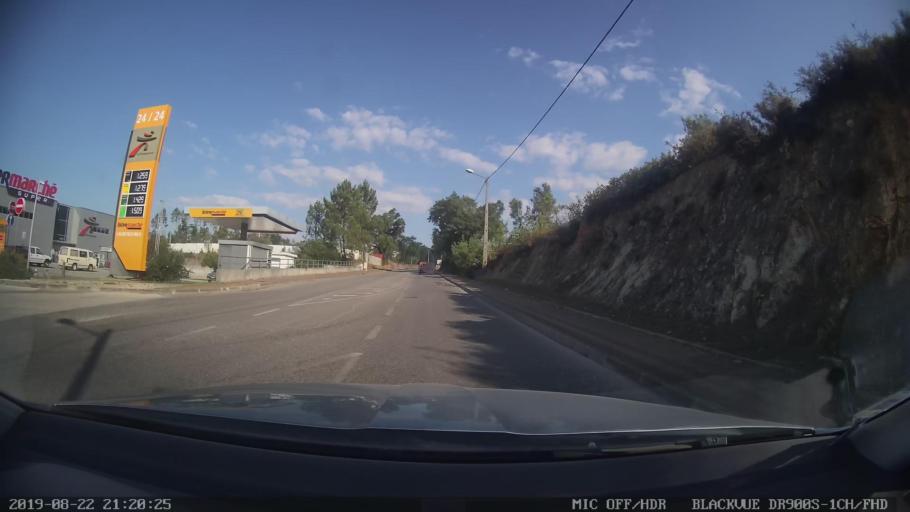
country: PT
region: Castelo Branco
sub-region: Serta
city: Serta
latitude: 39.8124
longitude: -8.1076
